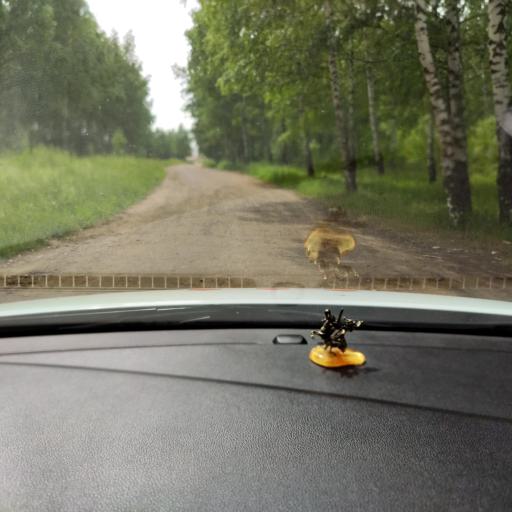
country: RU
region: Tatarstan
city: Staroye Arakchino
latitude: 55.8878
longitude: 49.0418
